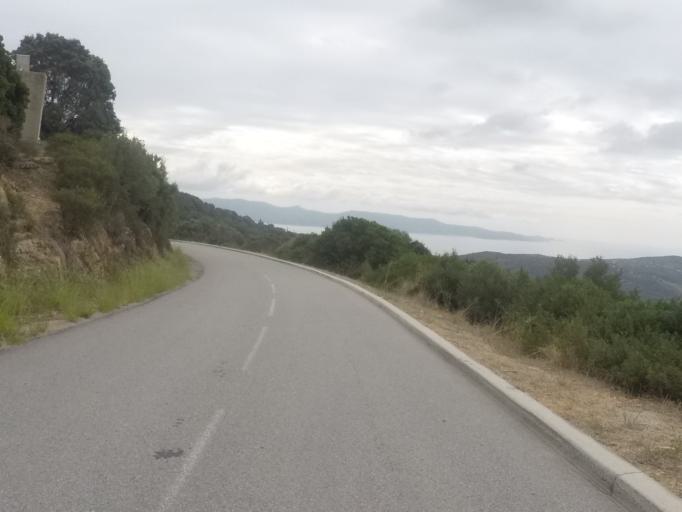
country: FR
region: Corsica
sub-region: Departement de la Corse-du-Sud
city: Pietrosella
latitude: 41.7653
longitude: 8.8121
